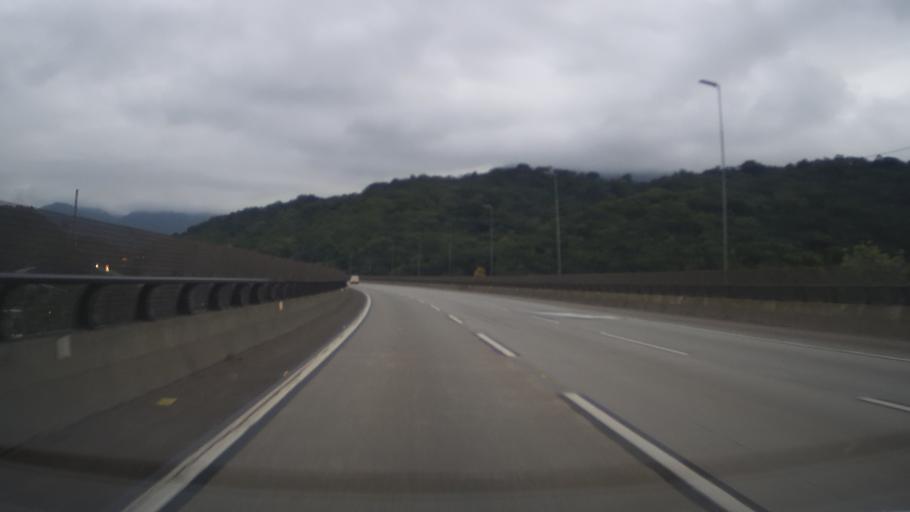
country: BR
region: Sao Paulo
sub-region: Cubatao
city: Cubatao
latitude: -23.9044
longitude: -46.4527
